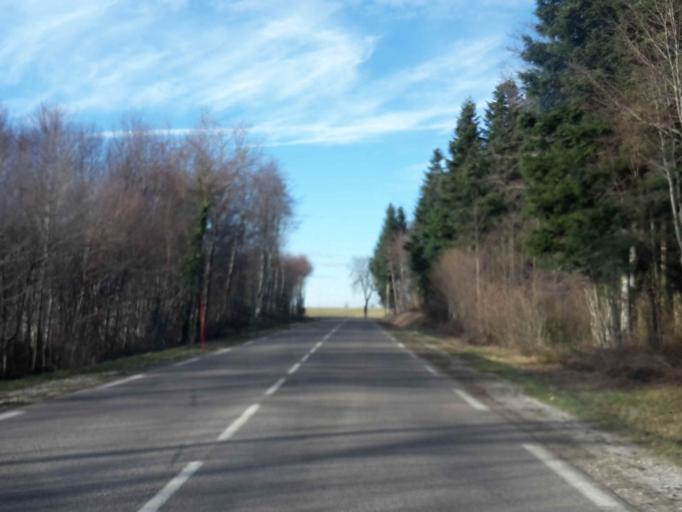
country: FR
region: Franche-Comte
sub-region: Departement du Doubs
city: Vercel-Villedieu-le-Camp
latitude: 47.2020
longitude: 6.3950
